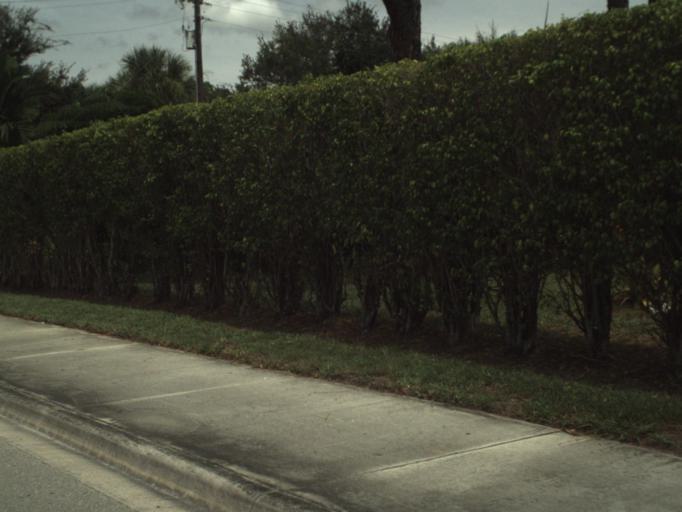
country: US
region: Florida
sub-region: Palm Beach County
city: North Palm Beach
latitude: 26.8449
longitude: -80.0761
